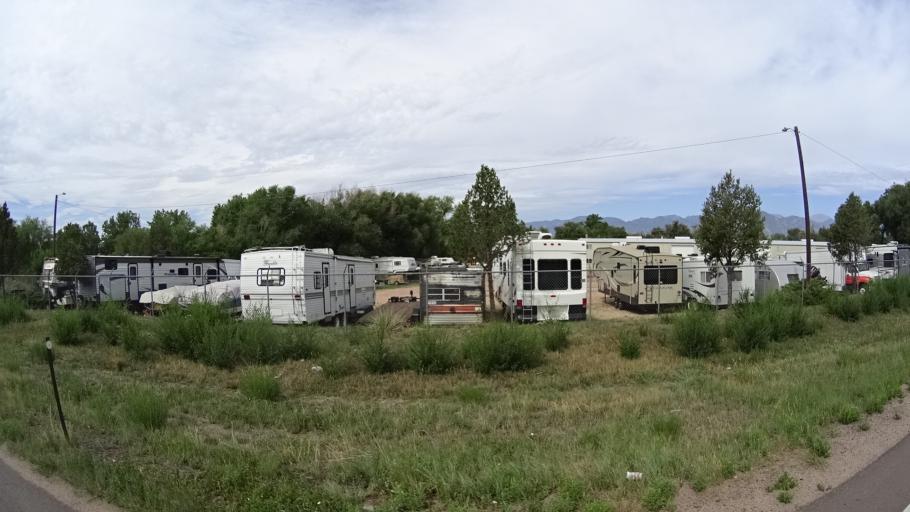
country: US
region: Colorado
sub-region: El Paso County
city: Fountain
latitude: 38.7043
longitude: -104.7096
